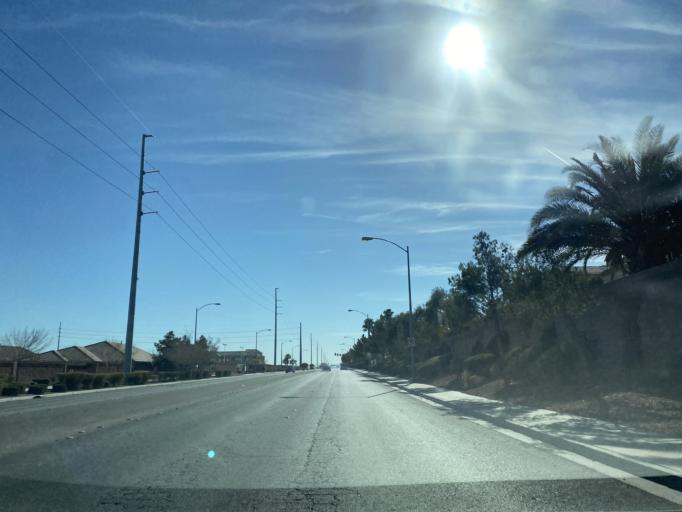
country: US
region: Nevada
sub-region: Clark County
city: North Las Vegas
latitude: 36.2313
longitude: -115.1435
